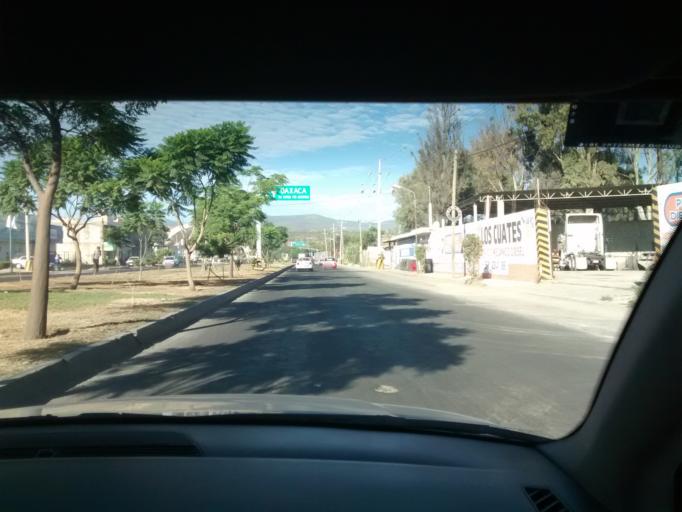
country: MX
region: Puebla
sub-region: Santiago Miahuatlan
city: San Jose Monte Chiquito
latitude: 18.4760
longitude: -97.4259
